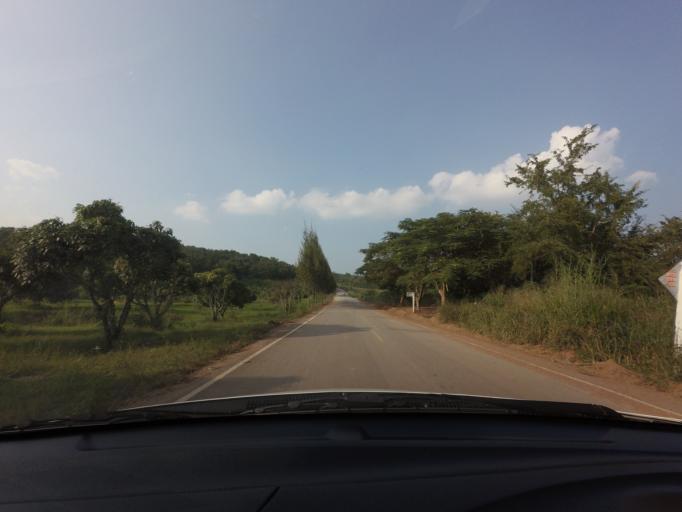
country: TH
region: Nakhon Ratchasima
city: Pak Chong
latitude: 14.5438
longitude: 101.5770
